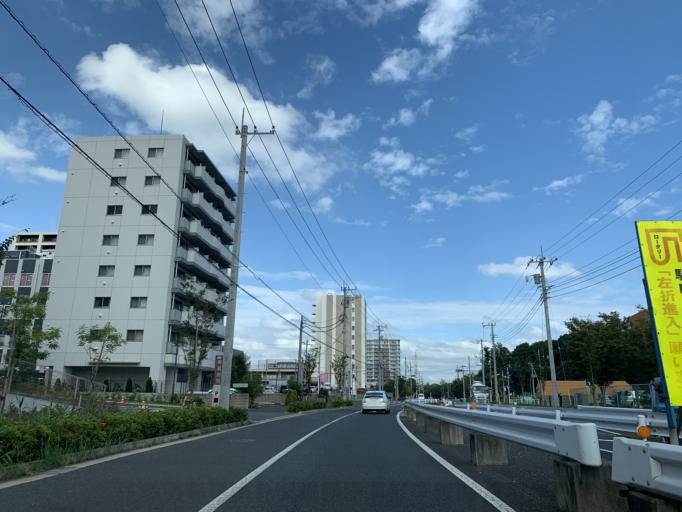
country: JP
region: Chiba
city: Nagareyama
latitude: 35.8530
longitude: 139.9166
